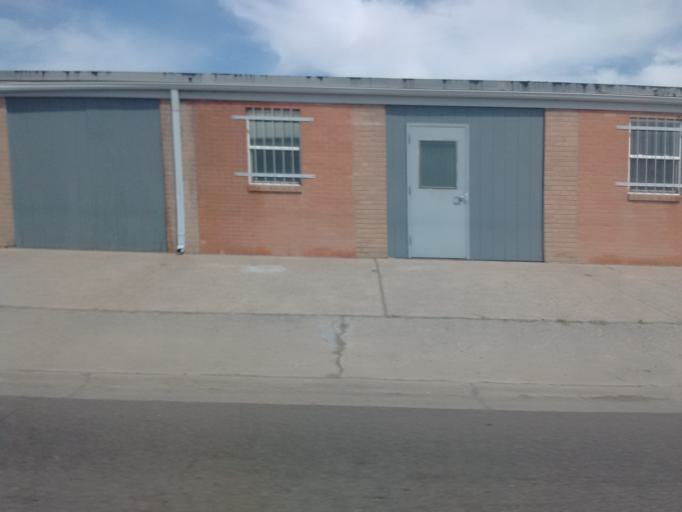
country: US
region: Colorado
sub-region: Mesa County
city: Grand Junction
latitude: 39.0617
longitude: -108.5563
